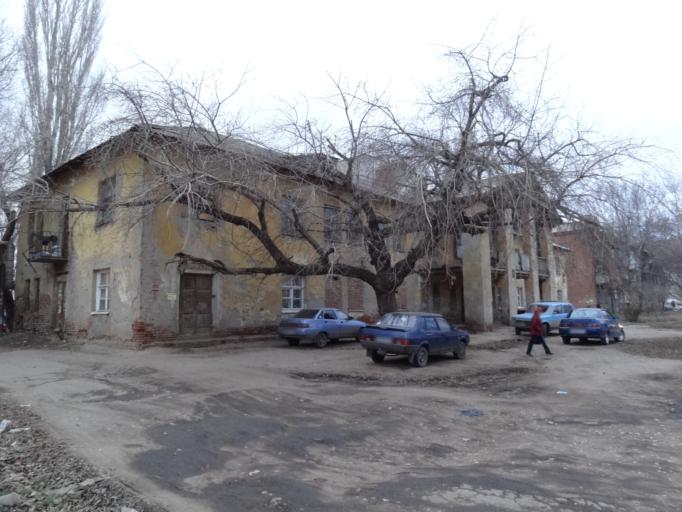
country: RU
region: Saratov
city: Engel's
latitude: 51.4689
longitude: 46.1080
